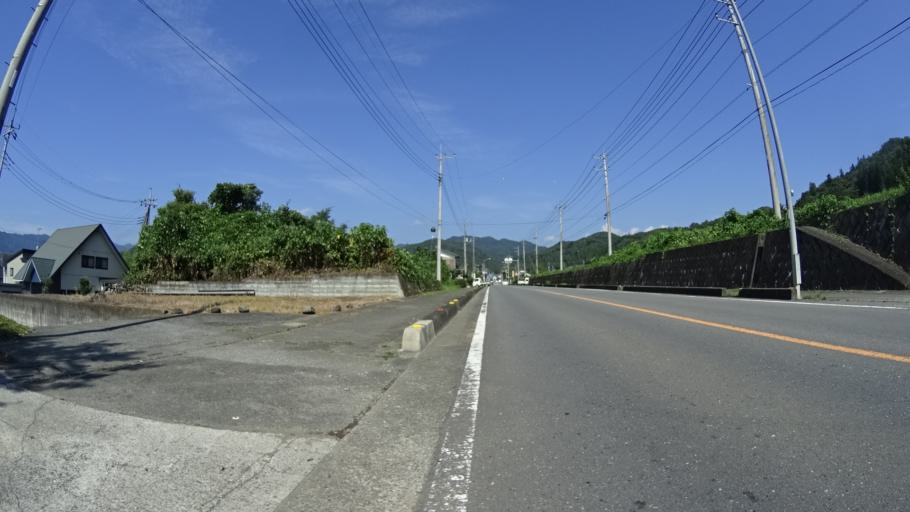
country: JP
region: Saitama
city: Chichibu
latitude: 36.0276
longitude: 138.9933
